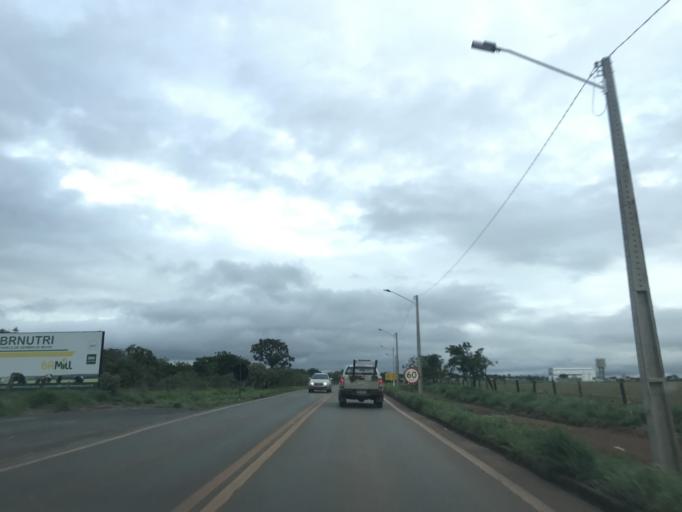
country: BR
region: Goias
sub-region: Luziania
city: Luziania
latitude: -16.2662
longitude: -47.9797
